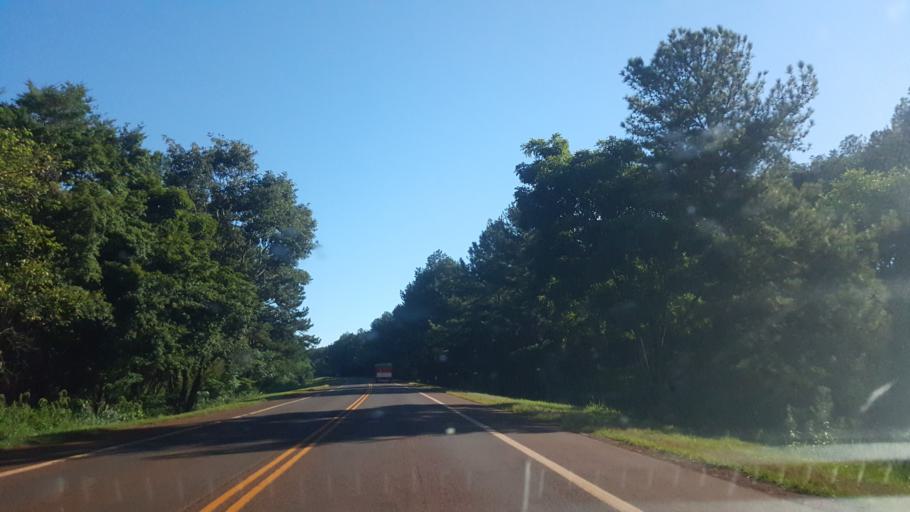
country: AR
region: Misiones
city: Puerto Libertad
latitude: -25.9076
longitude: -54.5686
